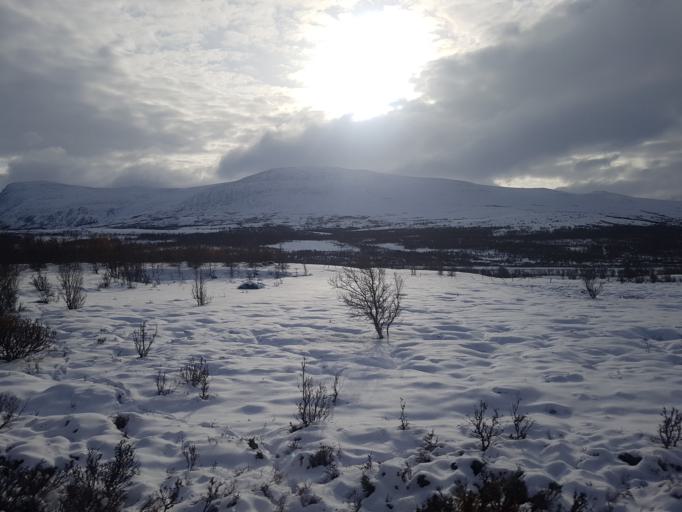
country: NO
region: Oppland
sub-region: Dovre
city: Dovre
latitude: 62.1394
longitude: 9.3266
